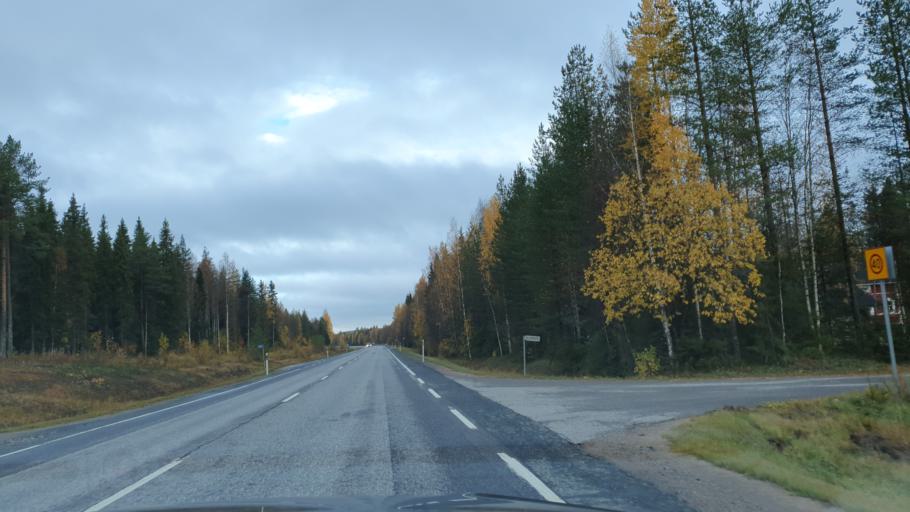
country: FI
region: Lapland
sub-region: Rovaniemi
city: Rovaniemi
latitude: 66.5692
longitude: 25.6367
